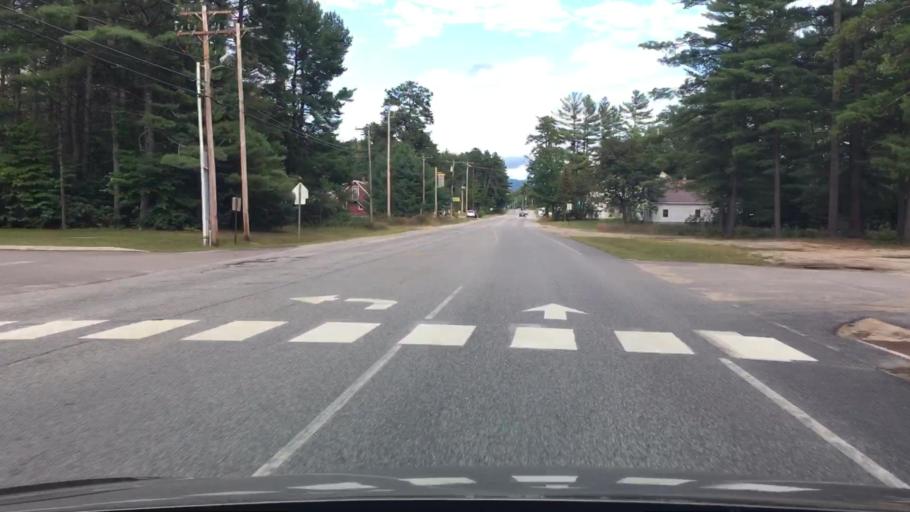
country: US
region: Maine
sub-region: Oxford County
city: Fryeburg
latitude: 44.0199
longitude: -70.9669
